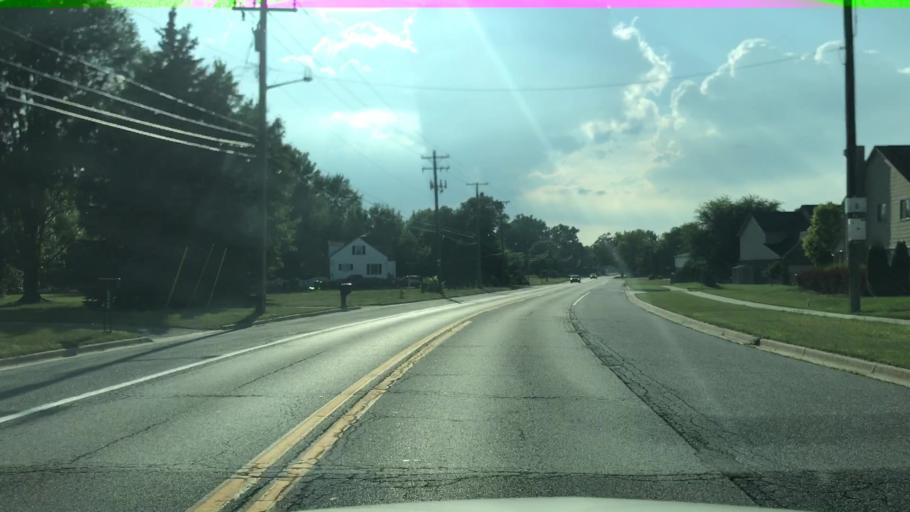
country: US
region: Michigan
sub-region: Macomb County
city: Fraser
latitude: 42.5771
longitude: -82.9625
